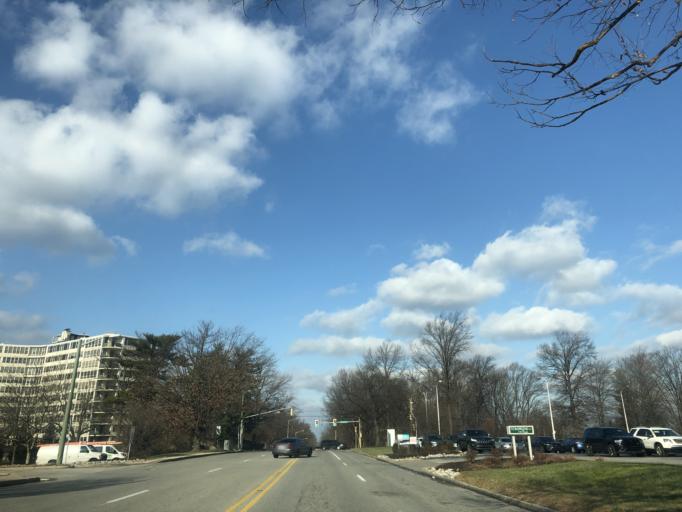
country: US
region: Pennsylvania
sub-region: Montgomery County
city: Bala-Cynwyd
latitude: 40.0048
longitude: -75.2213
